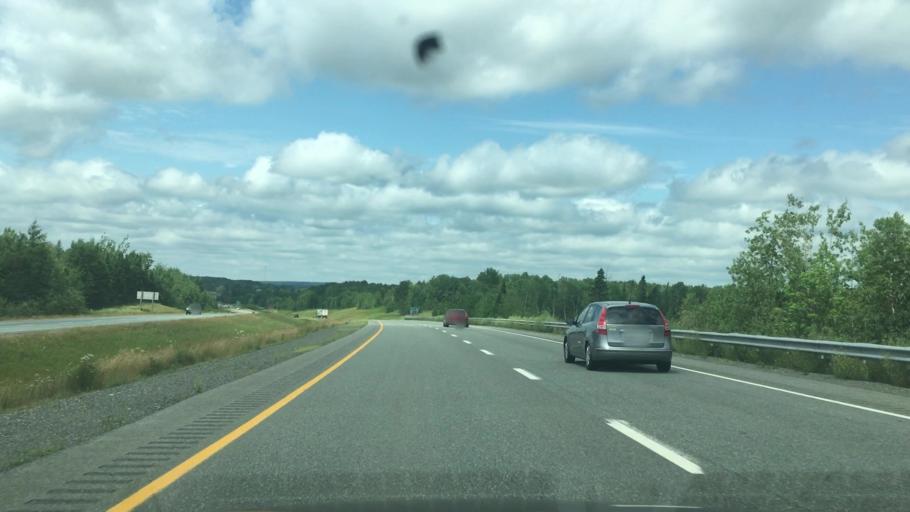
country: CA
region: Nova Scotia
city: Oxford
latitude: 45.7210
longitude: -63.8570
